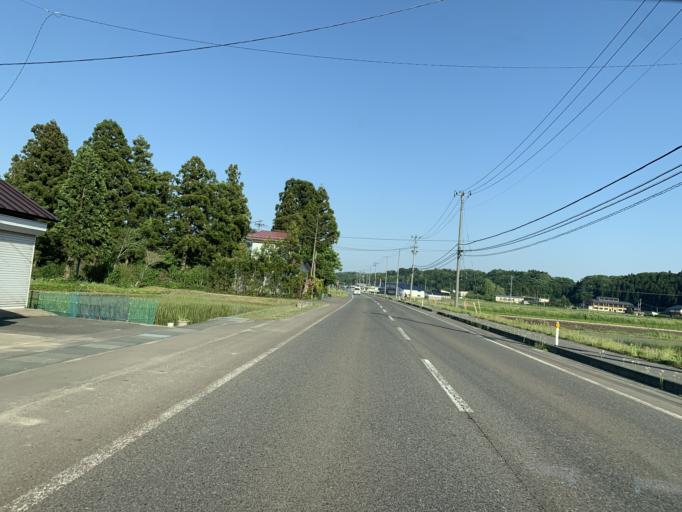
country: JP
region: Iwate
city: Kitakami
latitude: 39.2868
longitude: 141.0051
